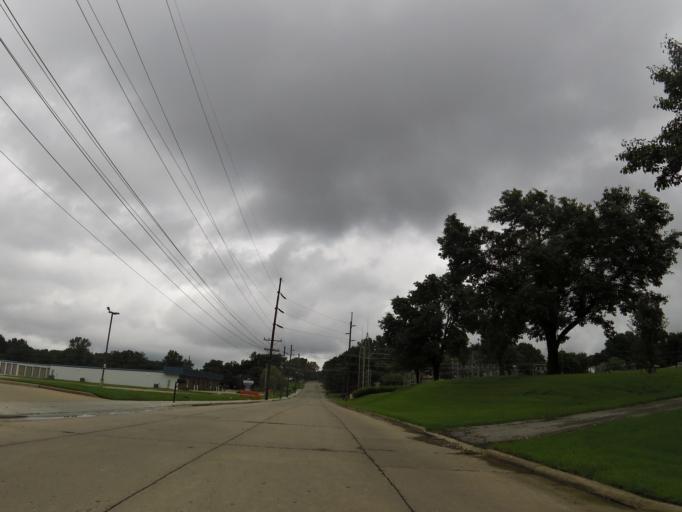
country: US
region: Missouri
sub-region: Cape Girardeau County
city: Cape Girardeau
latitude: 37.3168
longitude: -89.5468
